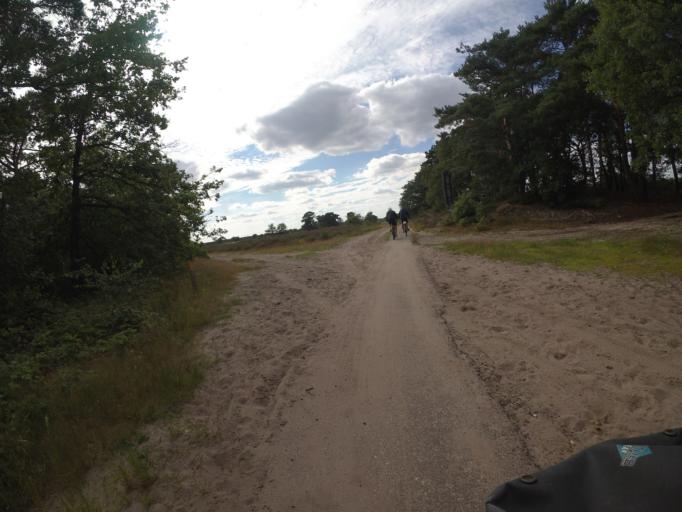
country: NL
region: North Brabant
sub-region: Gemeente Heeze-Leende
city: Heeze
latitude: 51.3749
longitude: 5.5369
